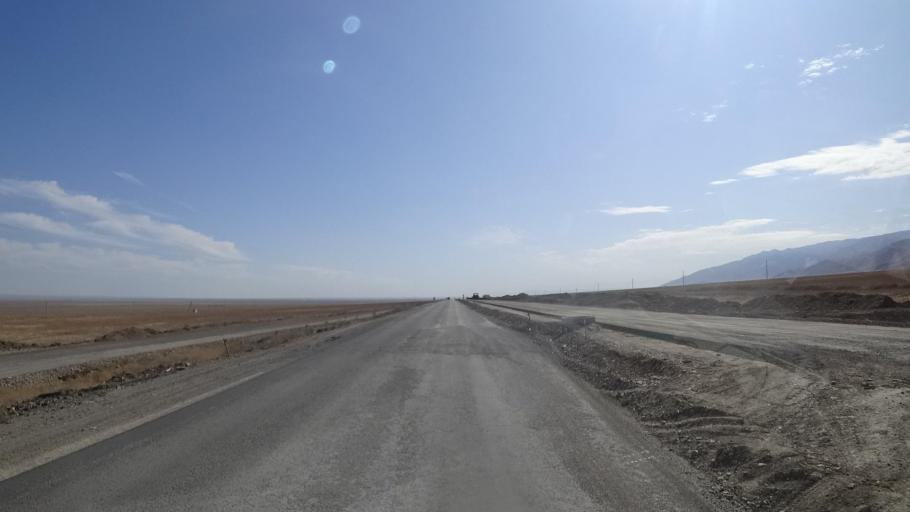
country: KG
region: Chuy
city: Ivanovka
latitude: 43.3831
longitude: 75.1858
